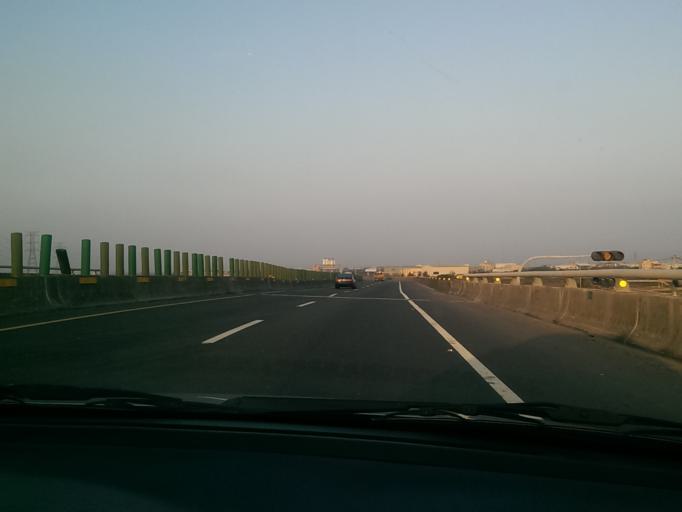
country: TW
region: Taiwan
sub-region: Changhua
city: Chang-hua
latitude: 24.1592
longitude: 120.4612
